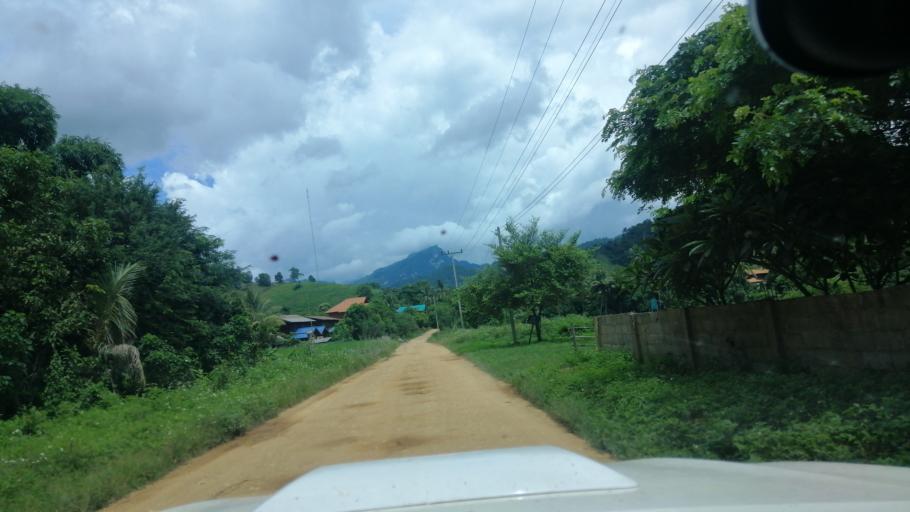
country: TH
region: Phayao
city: Phu Sang
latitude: 19.7089
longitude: 100.4896
